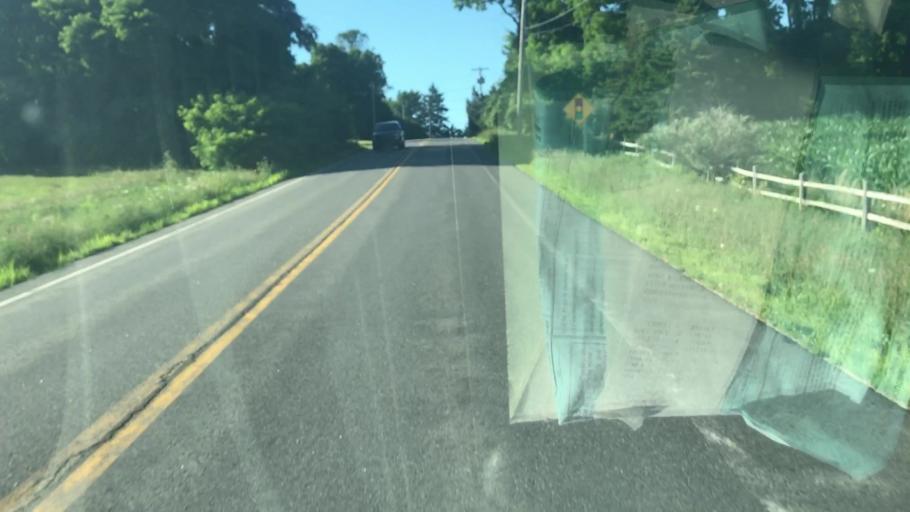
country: US
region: New York
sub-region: Onondaga County
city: Marcellus
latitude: 43.0322
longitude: -76.3643
